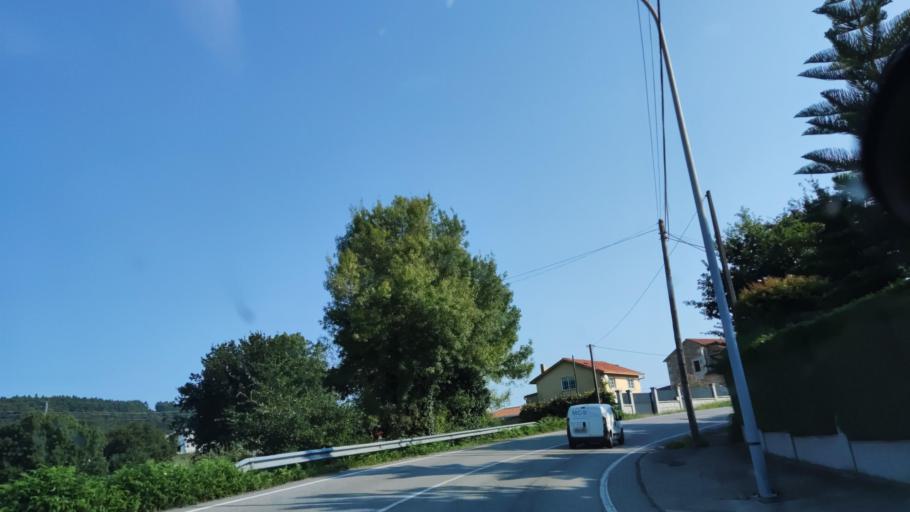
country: ES
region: Galicia
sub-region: Provincia da Coruna
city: Boiro
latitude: 42.6664
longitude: -8.8712
